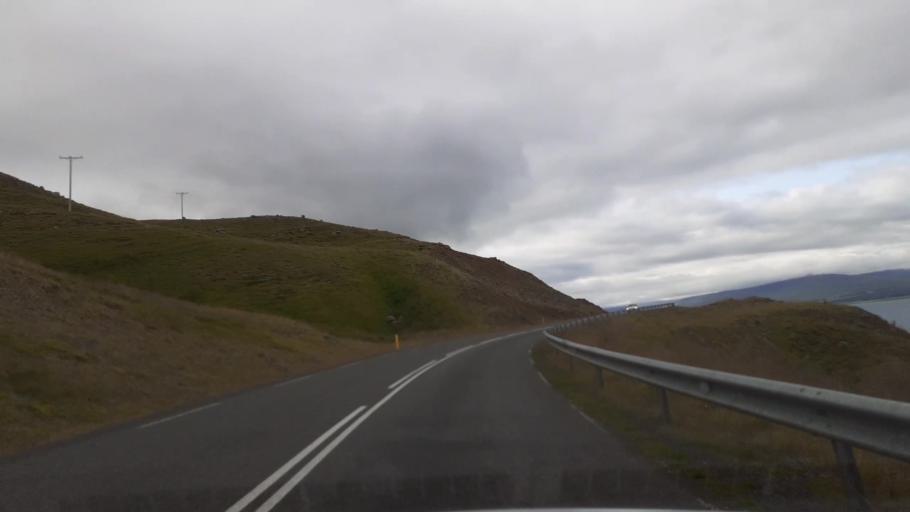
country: IS
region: Northeast
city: Akureyri
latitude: 65.8362
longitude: -18.0550
